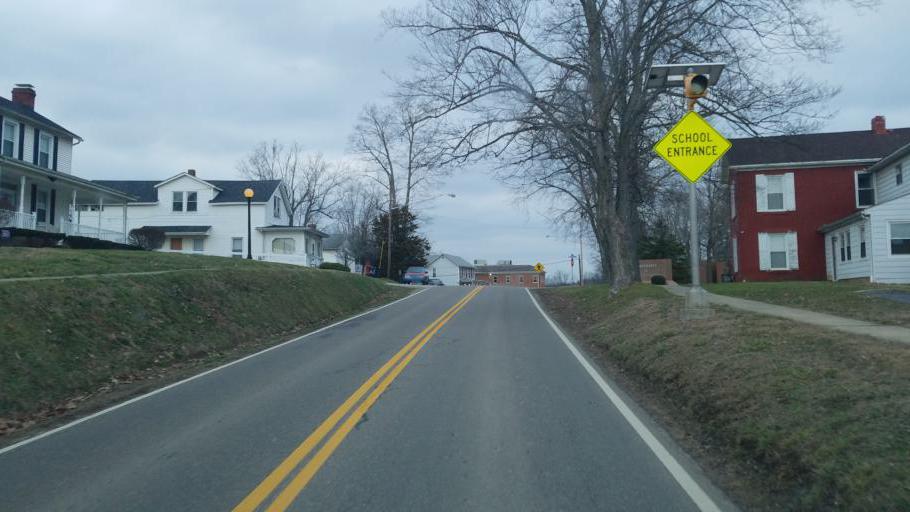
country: US
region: Ohio
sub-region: Gallia County
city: Gallipolis
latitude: 38.8805
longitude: -82.3807
